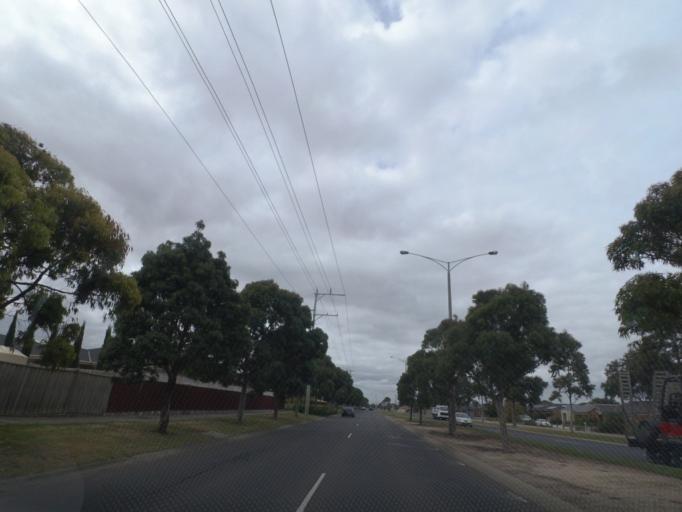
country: AU
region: Victoria
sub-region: Melton
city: Burnside Heights
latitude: -37.7244
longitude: 144.7550
